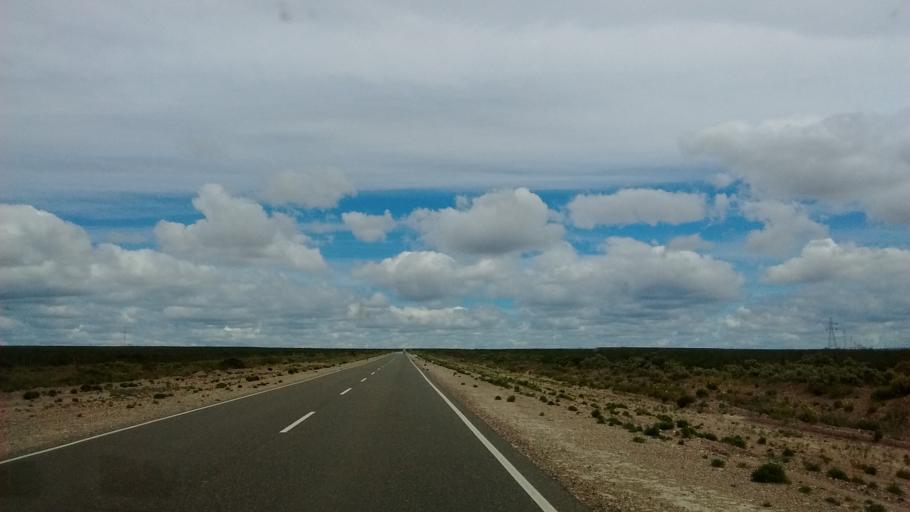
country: AR
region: Neuquen
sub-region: Departamento de Picun Leufu
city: Picun Leufu
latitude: -39.7443
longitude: -69.6093
